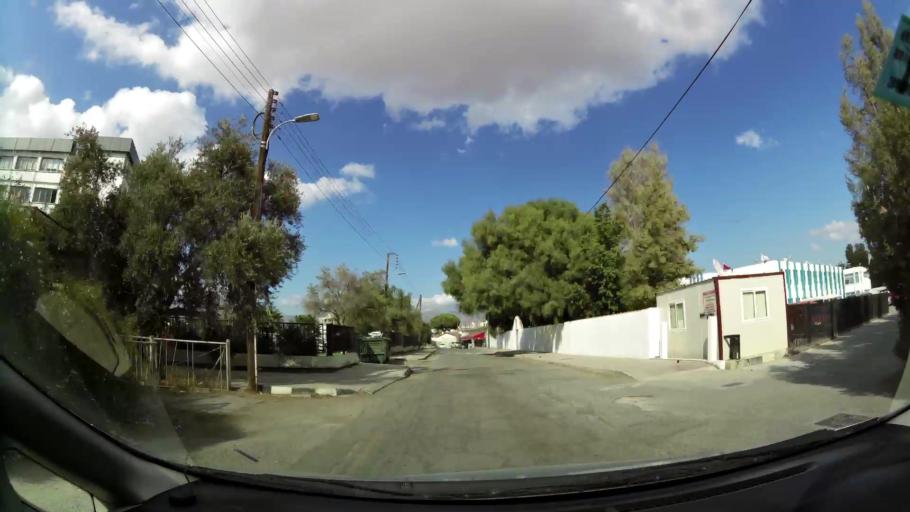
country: CY
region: Lefkosia
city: Nicosia
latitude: 35.1945
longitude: 33.3531
